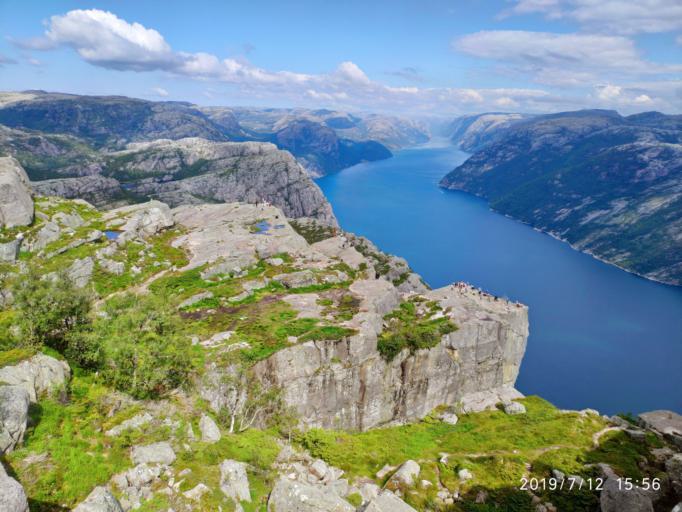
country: NO
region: Rogaland
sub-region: Forsand
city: Forsand
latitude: 58.9860
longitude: 6.1863
